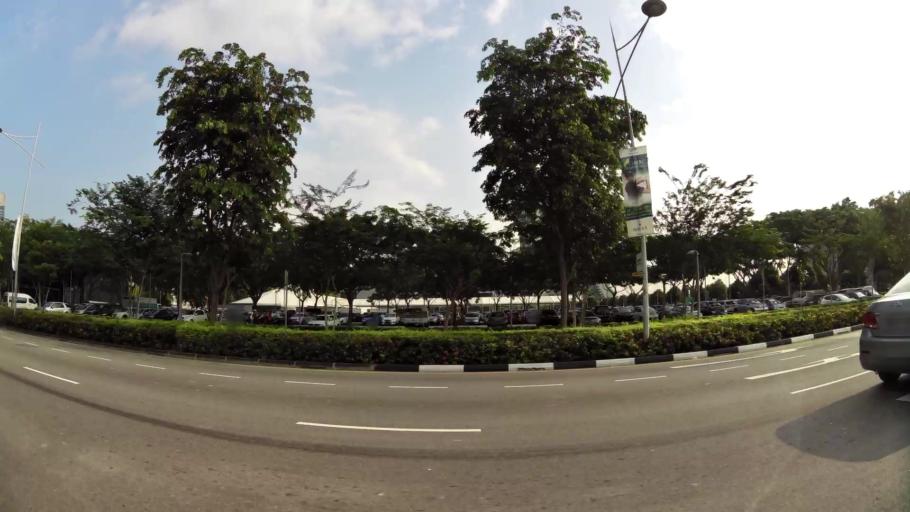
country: SG
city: Singapore
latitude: 1.2792
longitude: 103.8567
